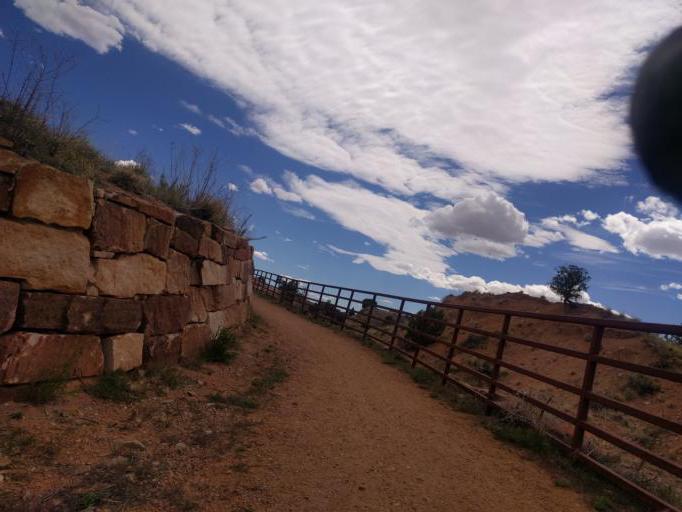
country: US
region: New Mexico
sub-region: Santa Fe County
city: Agua Fria
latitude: 35.6210
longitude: -105.9612
